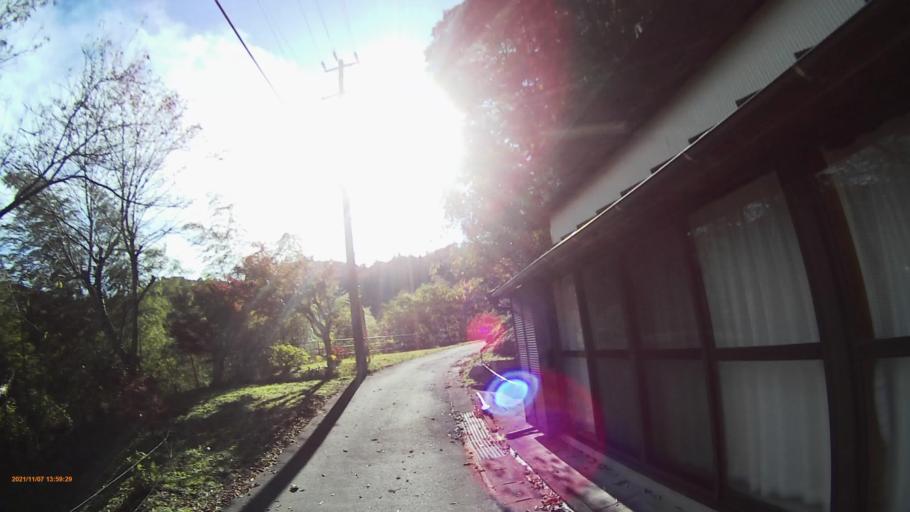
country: JP
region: Gifu
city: Mitake
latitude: 35.4249
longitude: 137.1881
